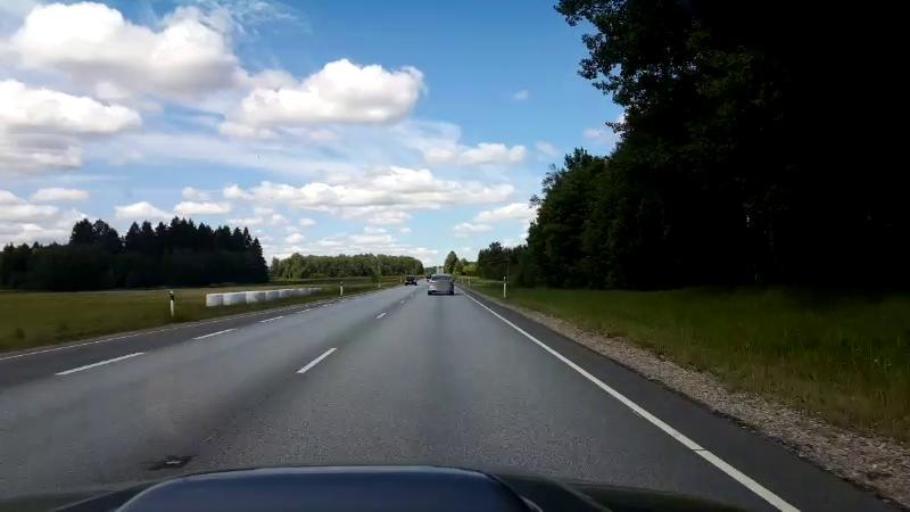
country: EE
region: Paernumaa
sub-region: Halinga vald
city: Parnu-Jaagupi
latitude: 58.5593
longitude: 24.5227
